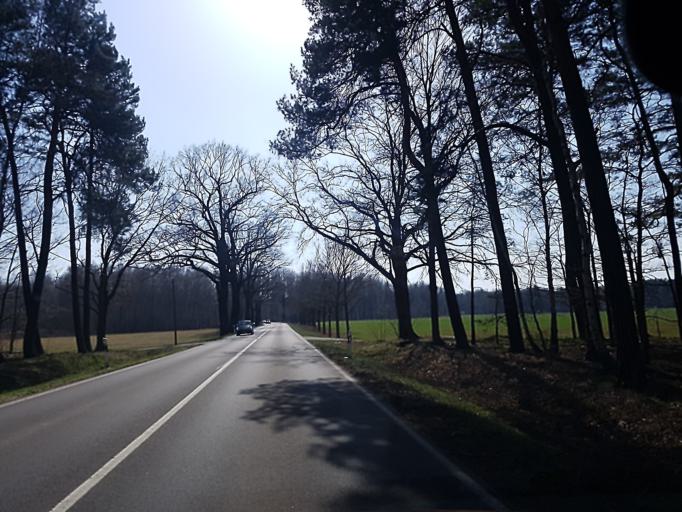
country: DE
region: Brandenburg
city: Tschernitz
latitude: 51.6493
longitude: 14.5862
